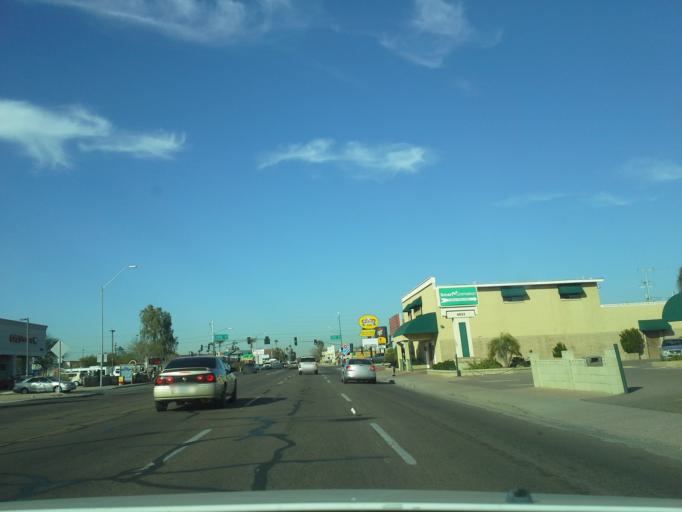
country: US
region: Arizona
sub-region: Maricopa County
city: Phoenix
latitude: 33.4936
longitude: -112.0998
